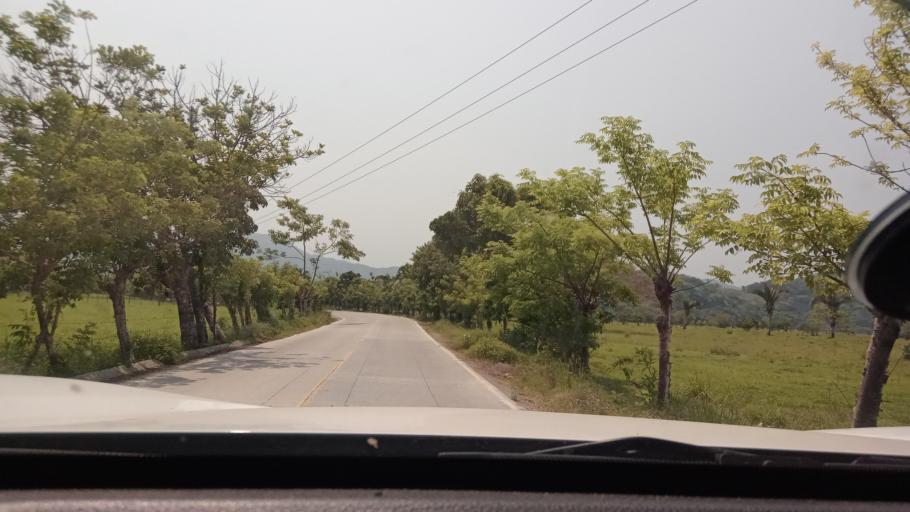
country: MX
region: Veracruz
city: Catemaco
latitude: 18.5614
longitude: -95.0394
